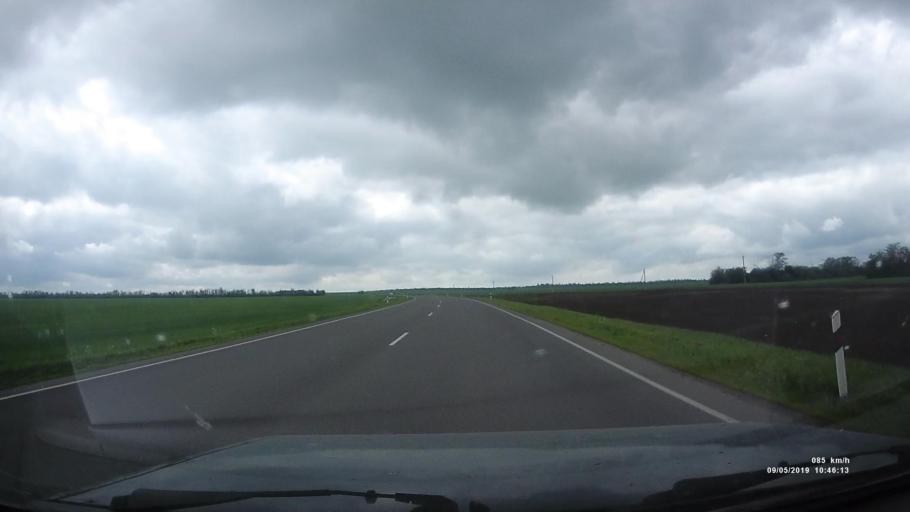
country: RU
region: Rostov
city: Peshkovo
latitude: 46.9872
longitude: 39.3577
